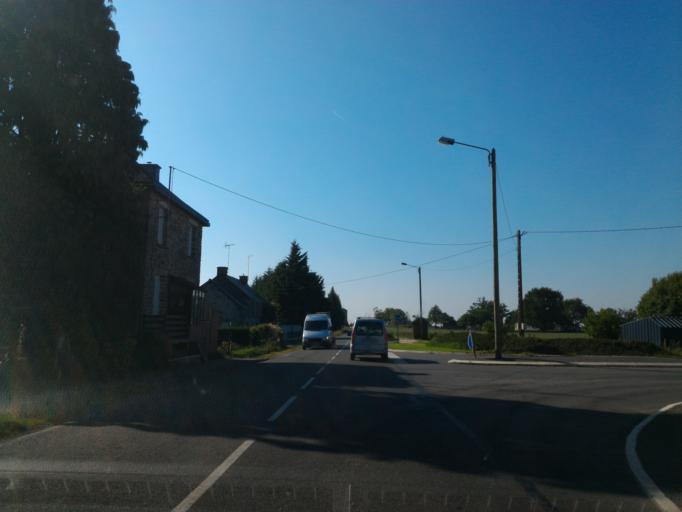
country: FR
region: Pays de la Loire
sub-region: Departement de la Mayenne
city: Juvigne
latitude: 48.2209
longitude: -1.0930
